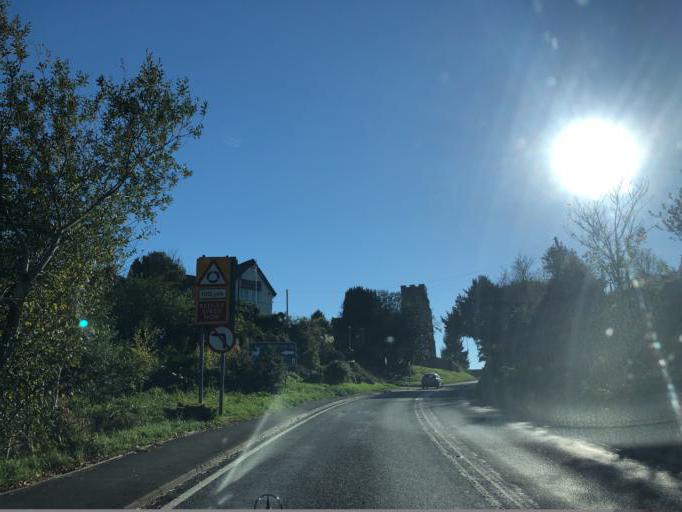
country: GB
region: England
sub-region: Warwickshire
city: Harbury
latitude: 52.2576
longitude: -1.4473
